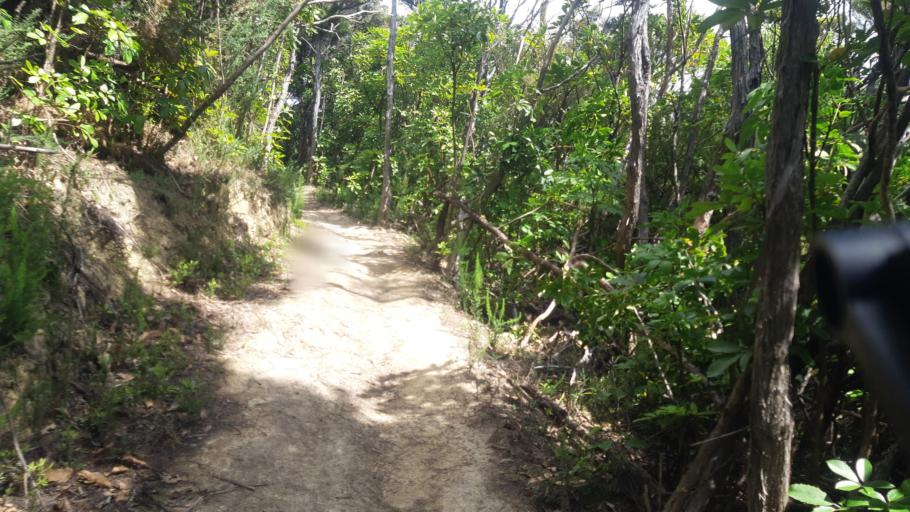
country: NZ
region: Marlborough
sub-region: Marlborough District
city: Picton
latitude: -41.2526
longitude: 174.0441
